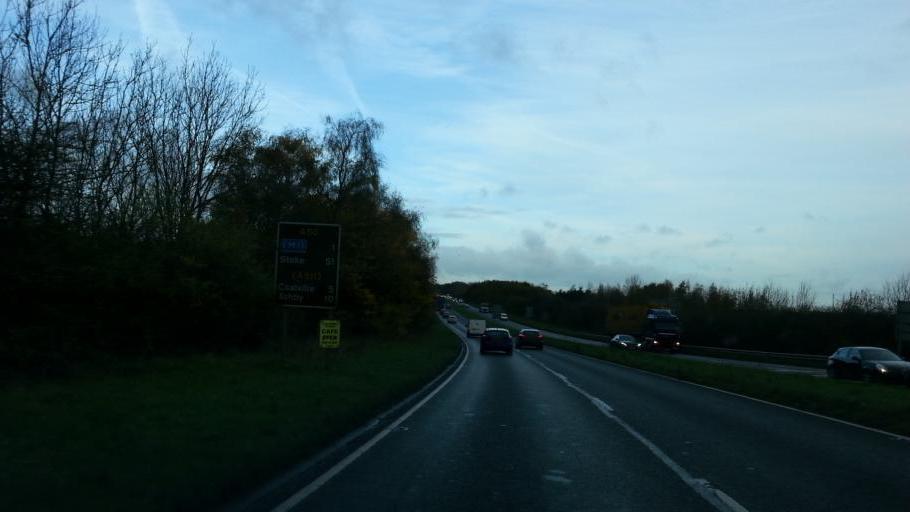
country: GB
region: England
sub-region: Leicestershire
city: Markfield
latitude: 52.6881
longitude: -1.2687
